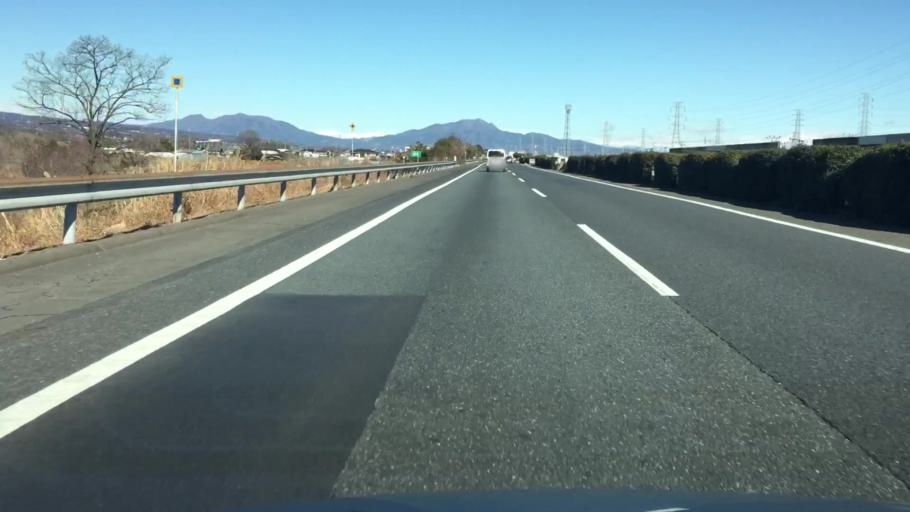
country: JP
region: Gunma
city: Maebashi-shi
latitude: 36.3906
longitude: 139.0257
